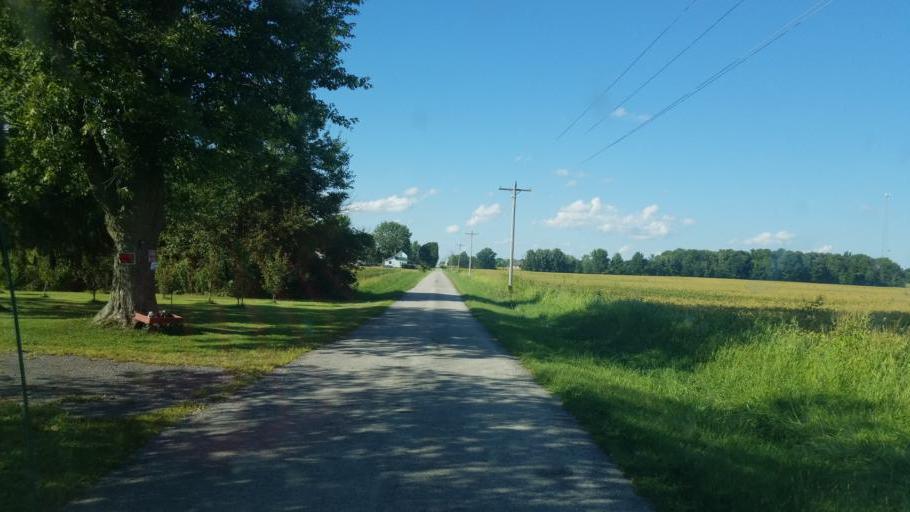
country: US
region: Ohio
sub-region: Marion County
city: Marion
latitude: 40.6240
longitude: -83.2694
